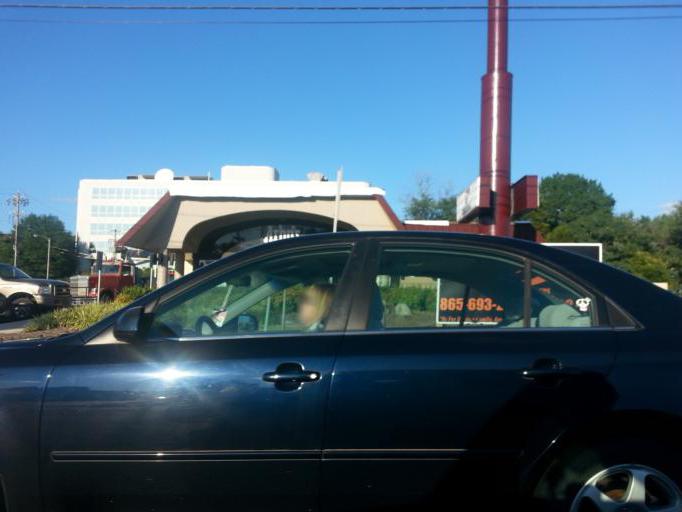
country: US
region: Tennessee
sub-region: Knox County
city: Farragut
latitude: 35.9224
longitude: -84.0930
